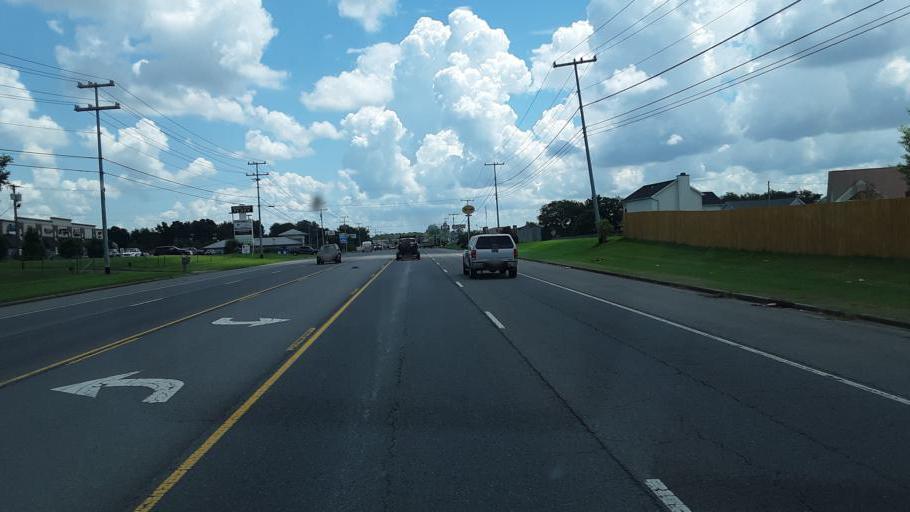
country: US
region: Tennessee
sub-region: Montgomery County
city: Clarksville
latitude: 36.6263
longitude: -87.3280
